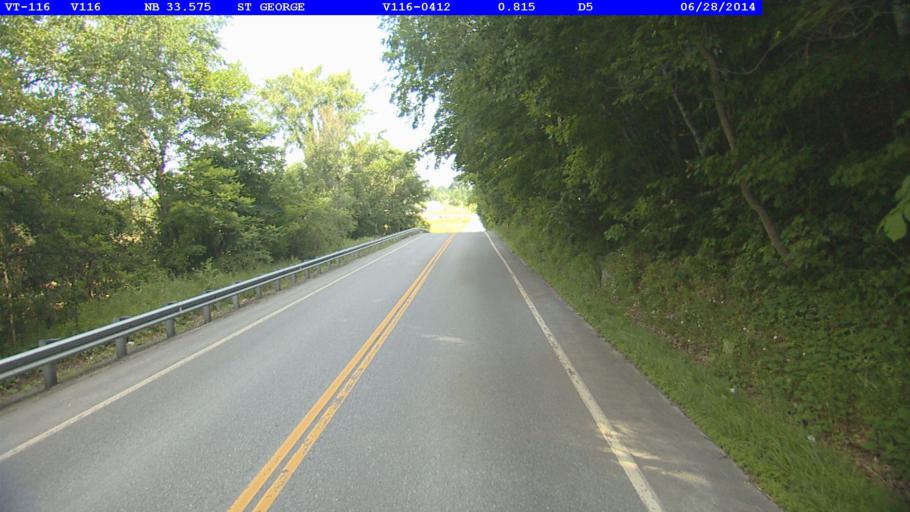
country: US
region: Vermont
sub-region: Chittenden County
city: Hinesburg
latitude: 44.3751
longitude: -73.1346
